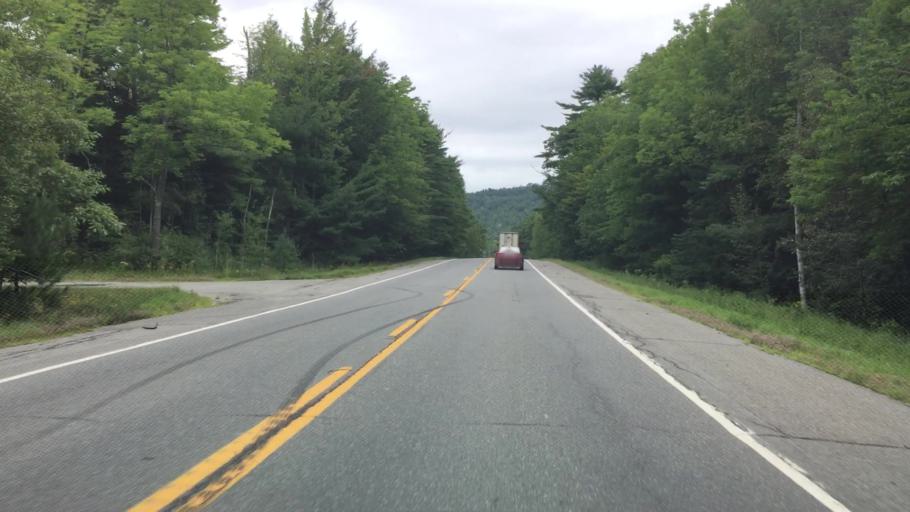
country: US
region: Maine
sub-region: Waldo County
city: Frankfort
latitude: 44.5701
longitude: -68.8652
